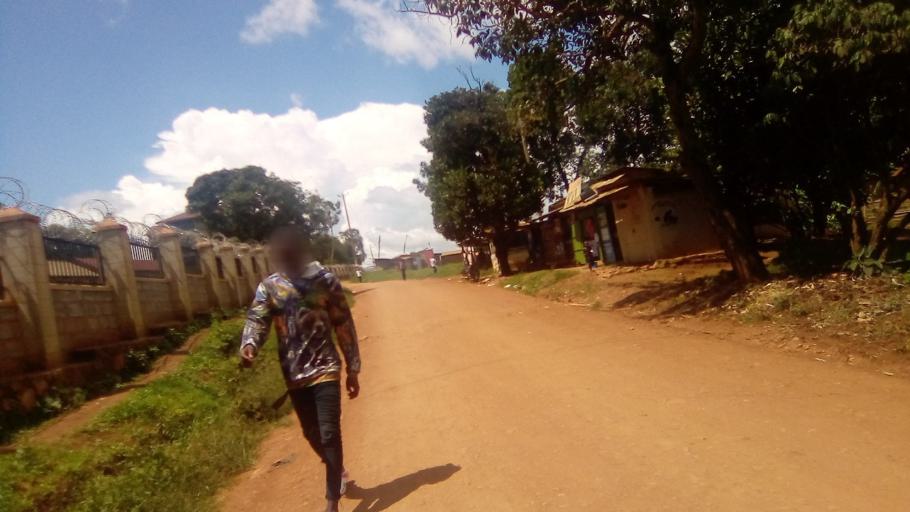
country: UG
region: Central Region
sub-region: Wakiso District
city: Entebbe
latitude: 0.0964
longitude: 32.5079
